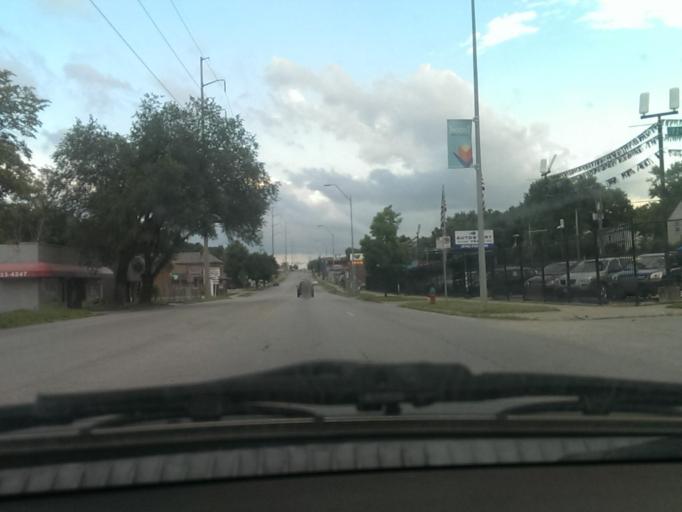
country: US
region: Kansas
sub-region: Johnson County
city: Mission Hills
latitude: 38.9963
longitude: -94.5755
